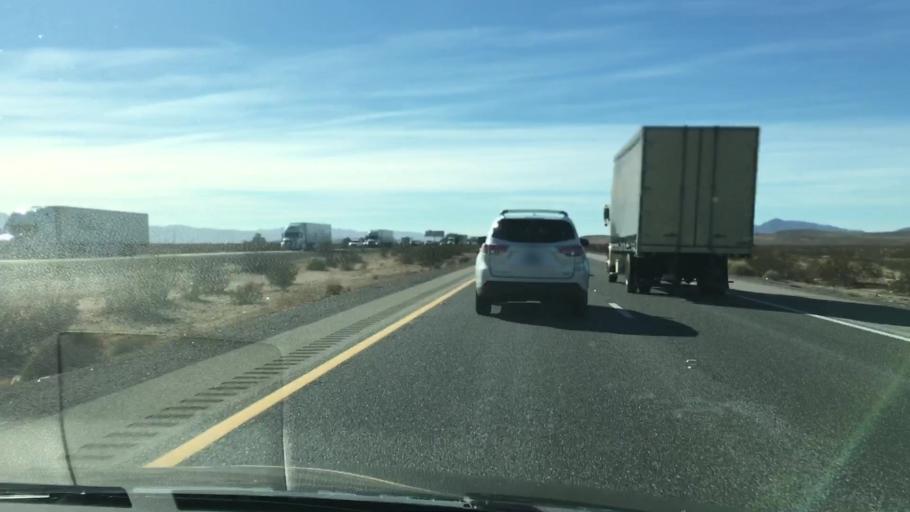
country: US
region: California
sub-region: San Bernardino County
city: Fort Irwin
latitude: 34.9822
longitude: -116.6027
